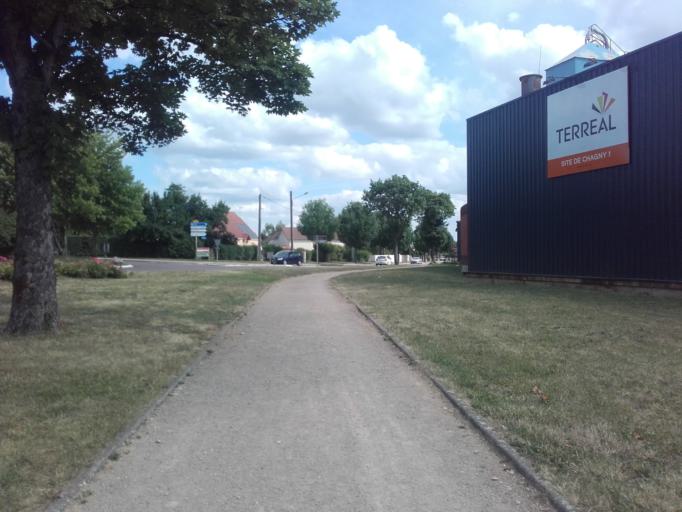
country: FR
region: Bourgogne
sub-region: Departement de Saone-et-Loire
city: Chagny
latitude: 46.9039
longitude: 4.7552
